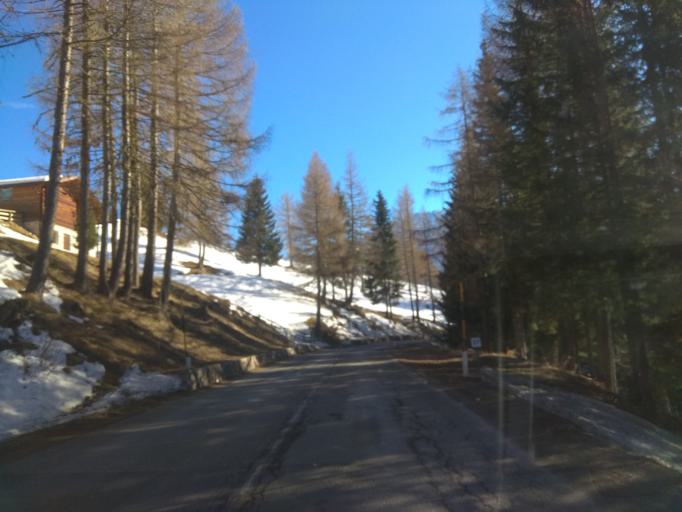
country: IT
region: Trentino-Alto Adige
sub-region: Bolzano
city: Nova Levante
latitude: 46.4268
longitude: 11.5976
